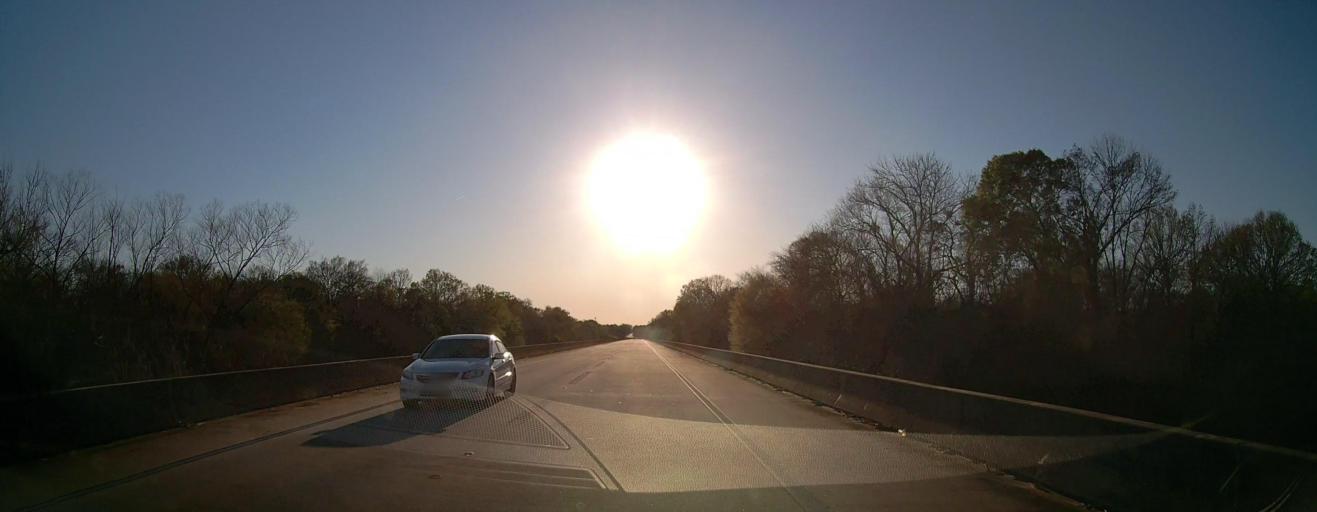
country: US
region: Georgia
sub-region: Wilcox County
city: Abbeville
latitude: 31.9967
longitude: -83.2791
